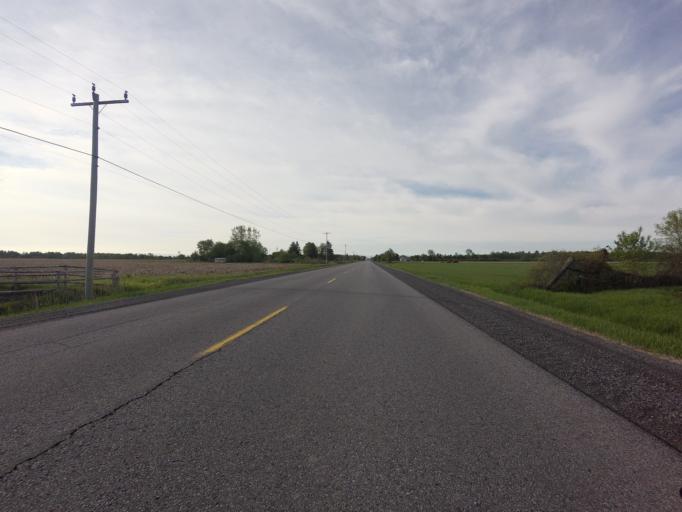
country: CA
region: Ontario
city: Ottawa
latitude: 45.2991
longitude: -75.4531
